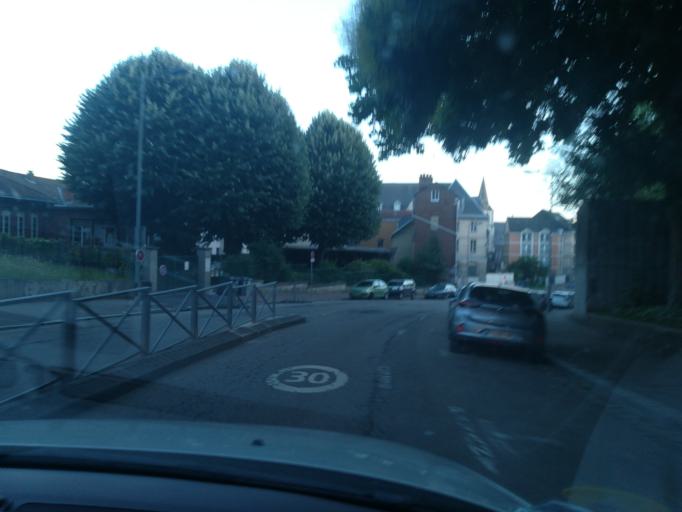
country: FR
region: Haute-Normandie
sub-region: Departement de la Seine-Maritime
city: Rouen
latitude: 49.4437
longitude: 1.1055
